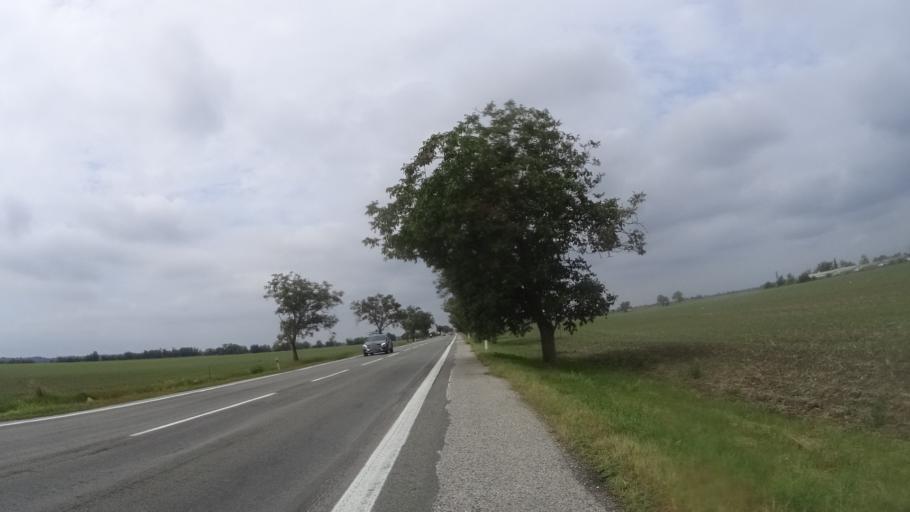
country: HU
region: Komarom-Esztergom
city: Acs
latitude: 47.7666
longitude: 18.0047
